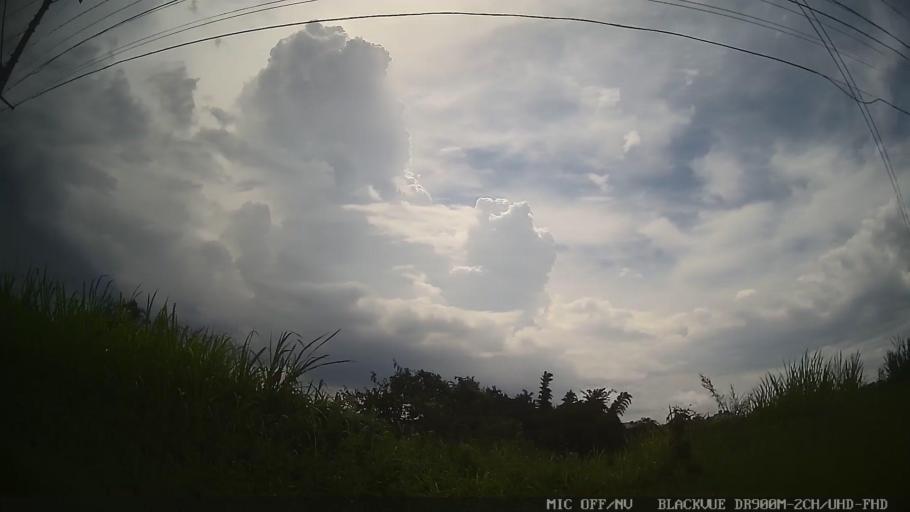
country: BR
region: Sao Paulo
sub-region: Suzano
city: Suzano
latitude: -23.4864
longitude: -46.2651
